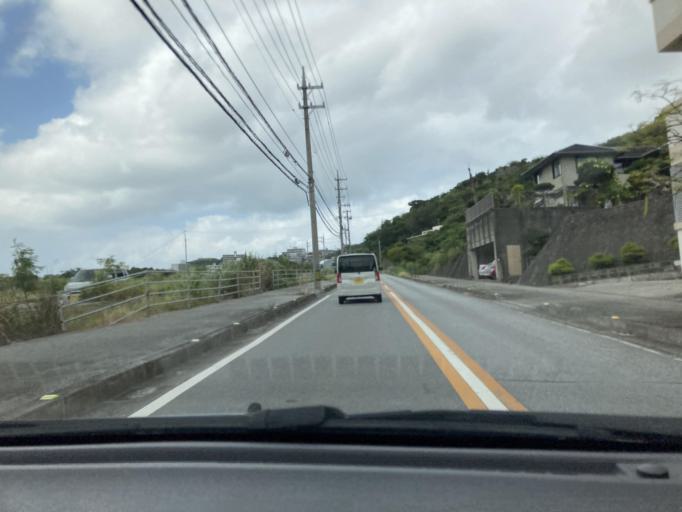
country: JP
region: Okinawa
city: Ginowan
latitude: 26.2399
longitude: 127.7570
